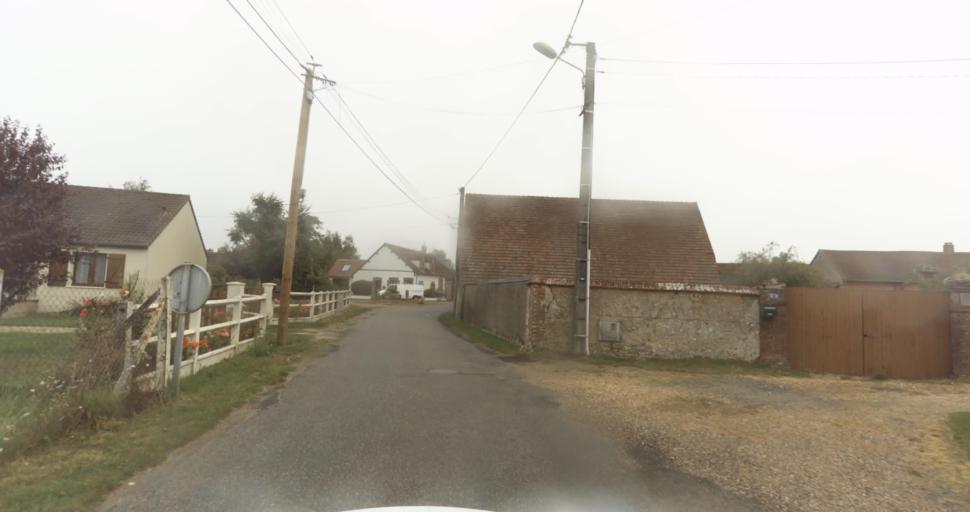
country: FR
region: Haute-Normandie
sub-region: Departement de l'Eure
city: Saint-Germain-sur-Avre
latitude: 48.7788
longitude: 1.2636
